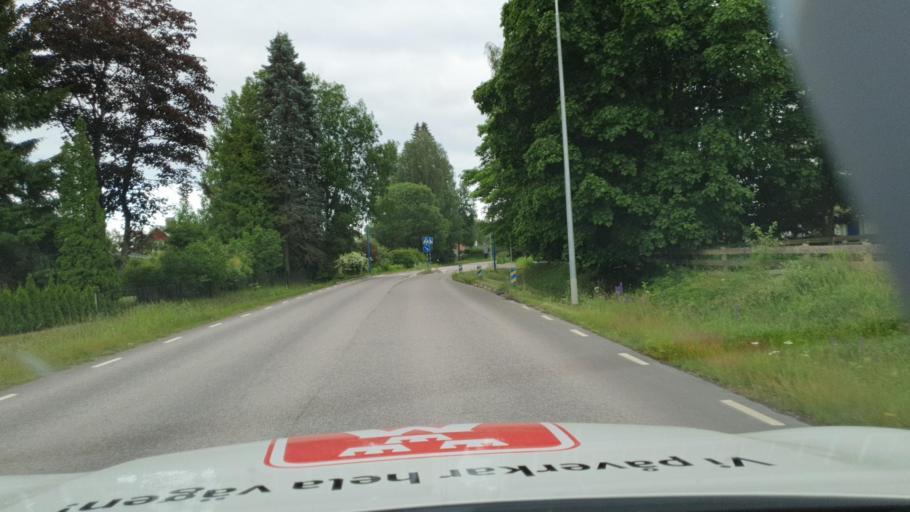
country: SE
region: Vaermland
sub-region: Karlstads Kommun
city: Karlstad
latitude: 59.4439
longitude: 13.4412
